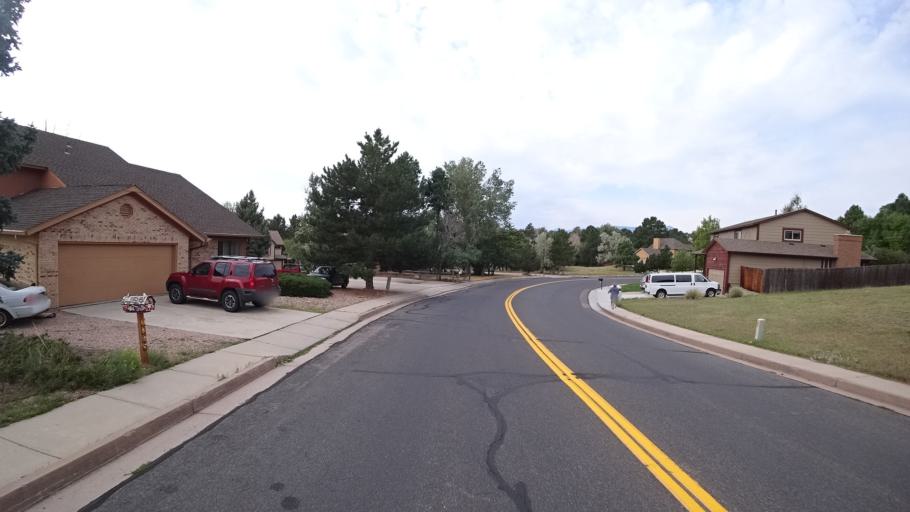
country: US
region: Colorado
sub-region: El Paso County
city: Air Force Academy
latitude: 38.9305
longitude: -104.8457
